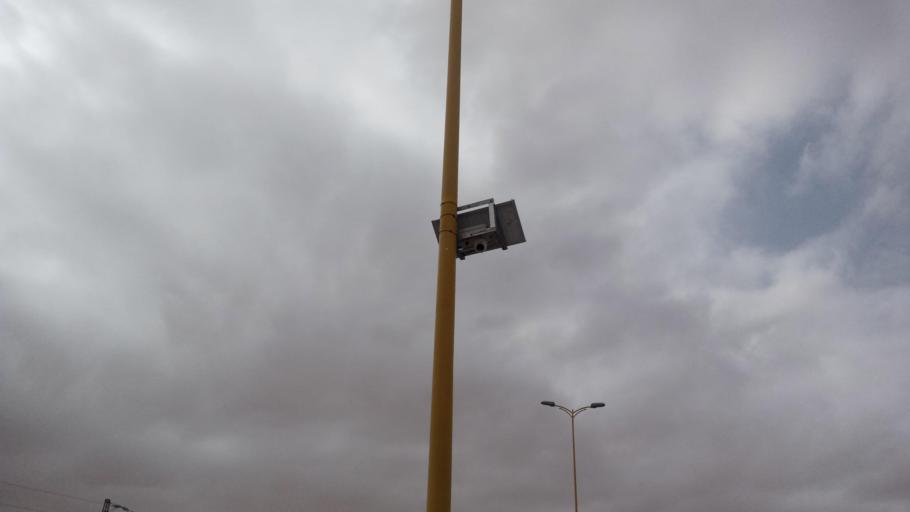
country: TN
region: Madanin
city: Medenine
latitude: 33.1914
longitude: 10.4433
